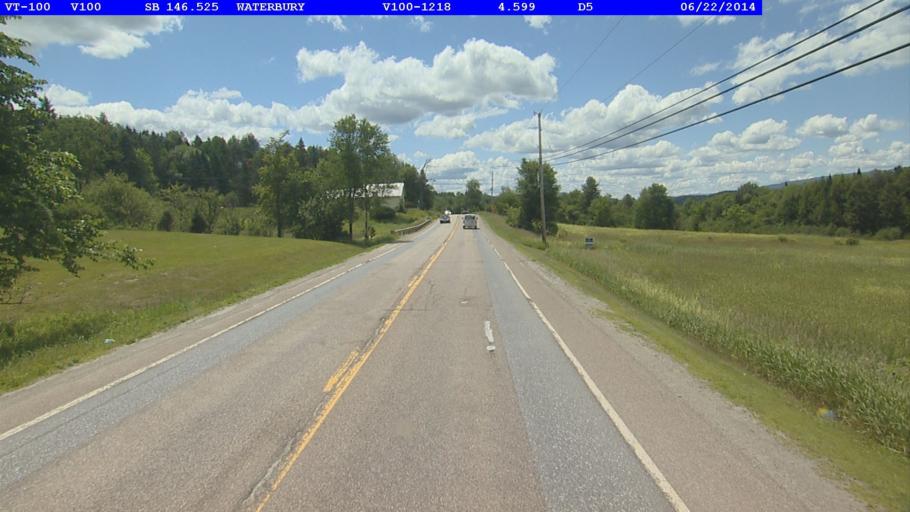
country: US
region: Vermont
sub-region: Washington County
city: Waterbury
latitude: 44.3953
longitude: -72.7192
